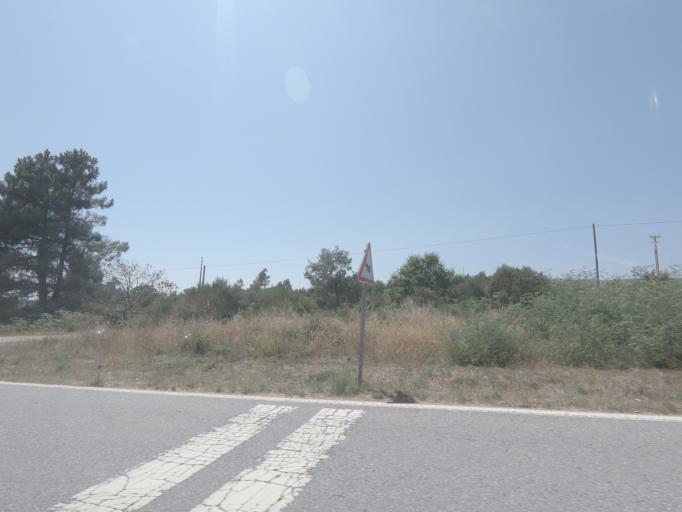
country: PT
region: Viseu
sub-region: Castro Daire
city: Castro Daire
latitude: 40.9653
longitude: -7.8845
